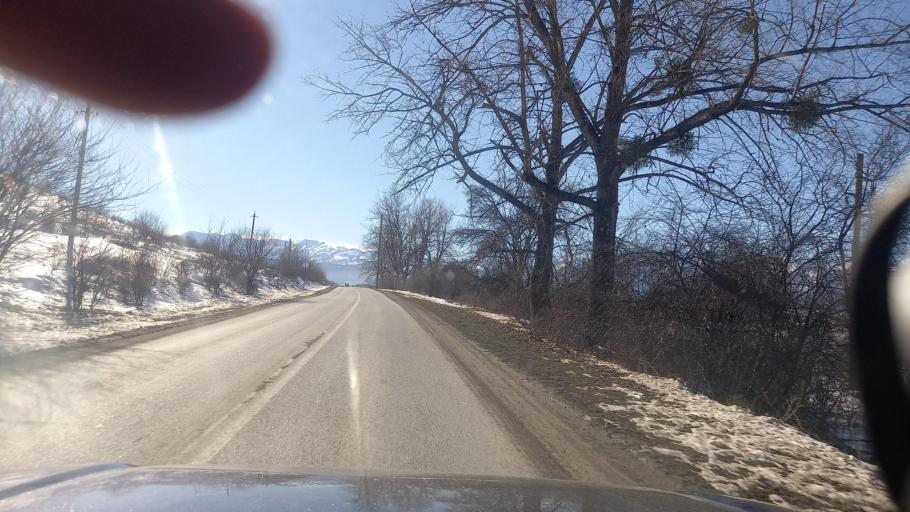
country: RU
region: North Ossetia
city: Chikola
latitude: 43.2167
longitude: 43.9239
